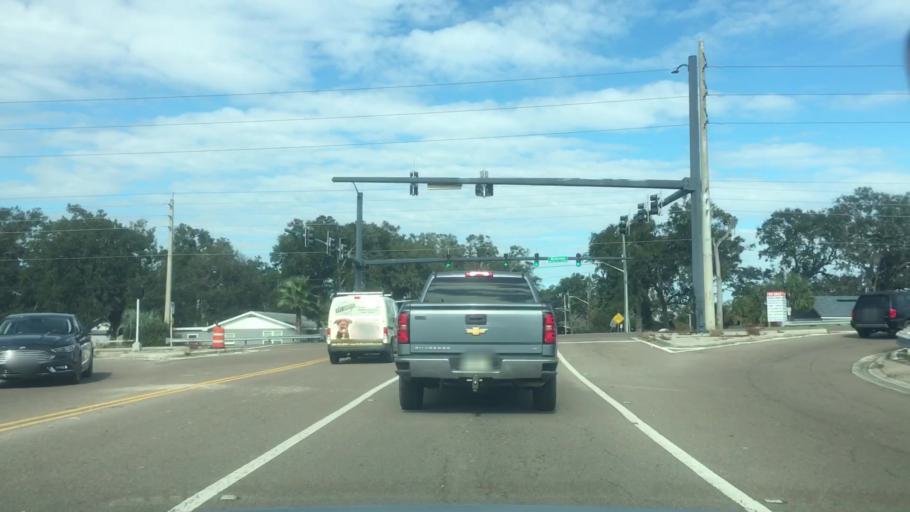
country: US
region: Florida
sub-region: Duval County
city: Atlantic Beach
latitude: 30.3577
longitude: -81.4629
